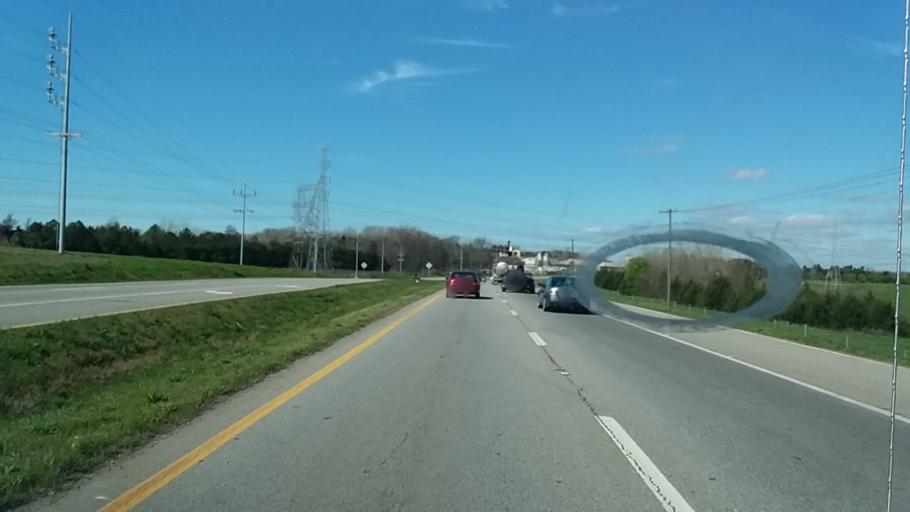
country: US
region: Alabama
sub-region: Morgan County
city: Trinity
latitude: 34.6201
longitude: -87.0705
